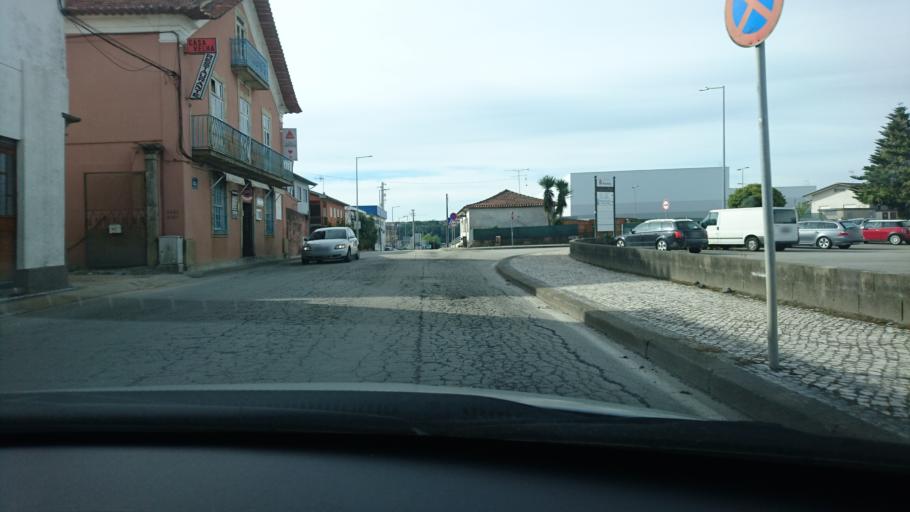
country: PT
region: Aveiro
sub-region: Oliveira de Azemeis
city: Oliveira de Azemeis
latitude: 40.8523
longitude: -8.4804
